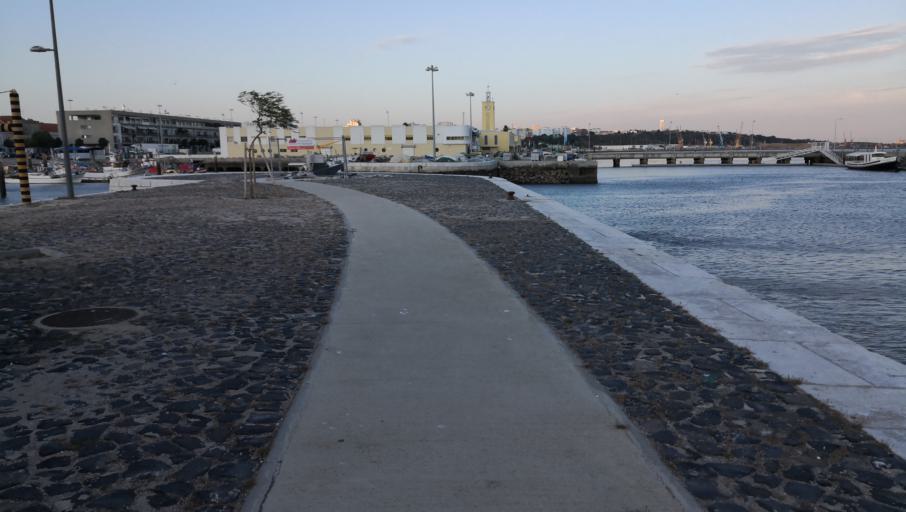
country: PT
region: Setubal
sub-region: Setubal
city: Setubal
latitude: 38.5189
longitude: -8.9002
